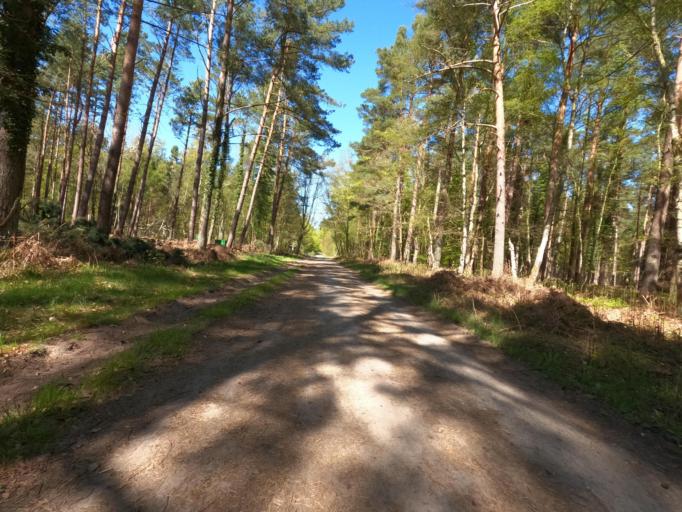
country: DE
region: Mecklenburg-Vorpommern
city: Born
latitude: 54.4150
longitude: 12.5326
